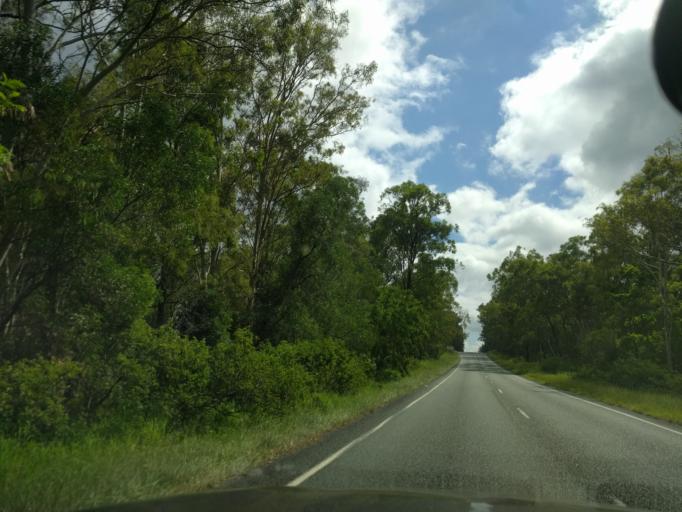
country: AU
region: Queensland
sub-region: Logan
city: Cedar Vale
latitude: -27.8560
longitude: 153.0081
